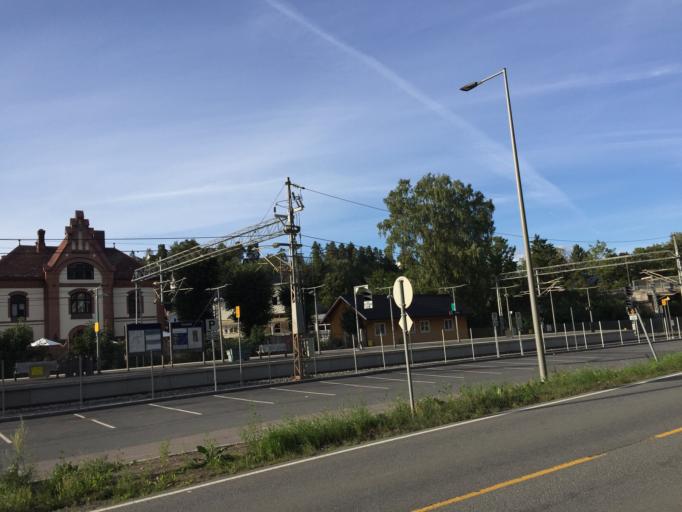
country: NO
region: Akershus
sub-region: Baerum
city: Lysaker
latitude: 59.9079
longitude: 10.6080
